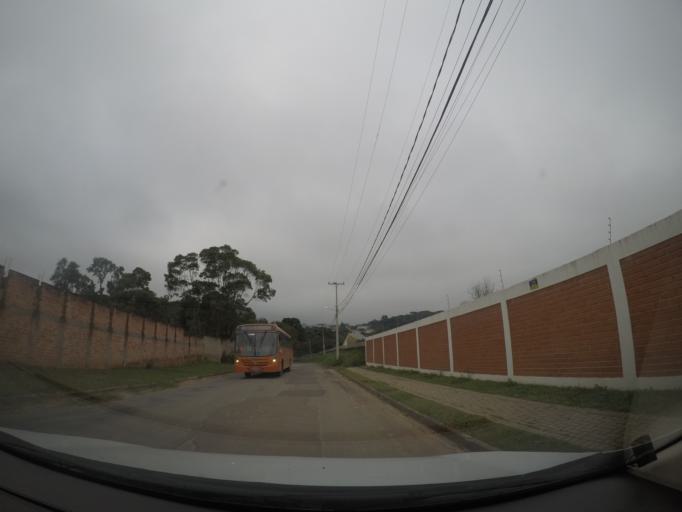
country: BR
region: Parana
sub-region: Colombo
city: Colombo
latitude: -25.3297
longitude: -49.2515
